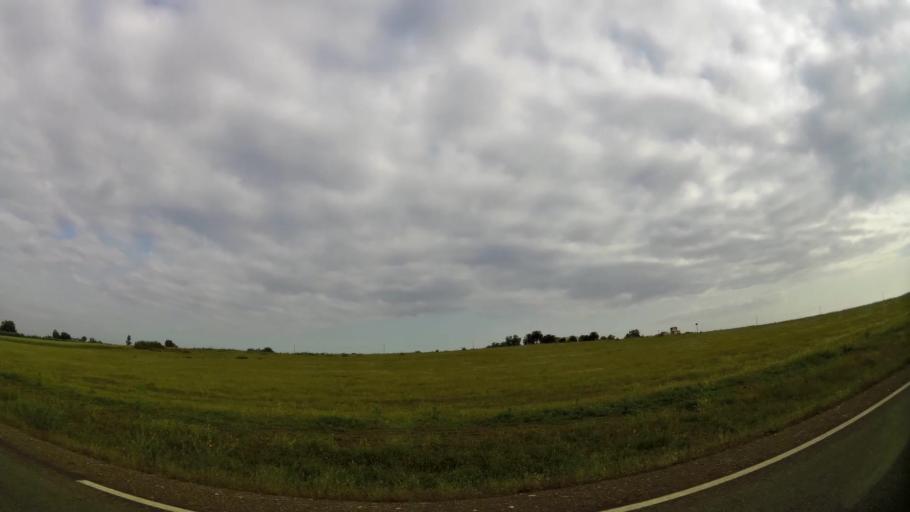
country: MA
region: Rabat-Sale-Zemmour-Zaer
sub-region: Khemisset
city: Khemisset
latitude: 33.7554
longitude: -6.1900
